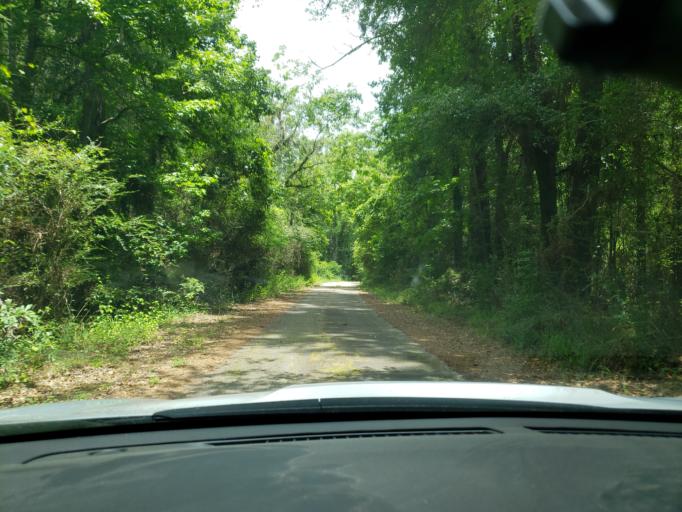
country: US
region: Alabama
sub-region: Escambia County
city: East Brewton
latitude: 31.1038
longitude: -86.9351
